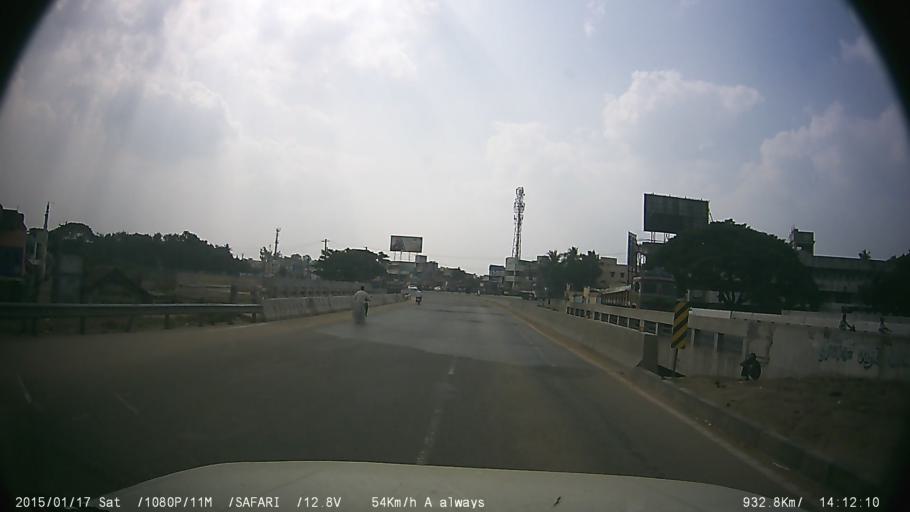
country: IN
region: Tamil Nadu
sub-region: Vellore
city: Ambur
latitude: 12.7892
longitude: 78.7254
